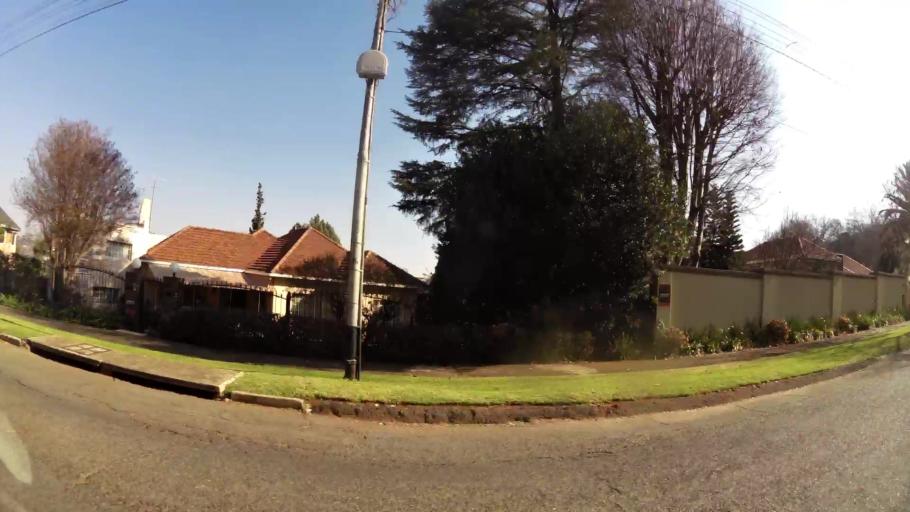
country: ZA
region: Gauteng
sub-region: City of Johannesburg Metropolitan Municipality
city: Johannesburg
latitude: -26.1716
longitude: 28.1046
